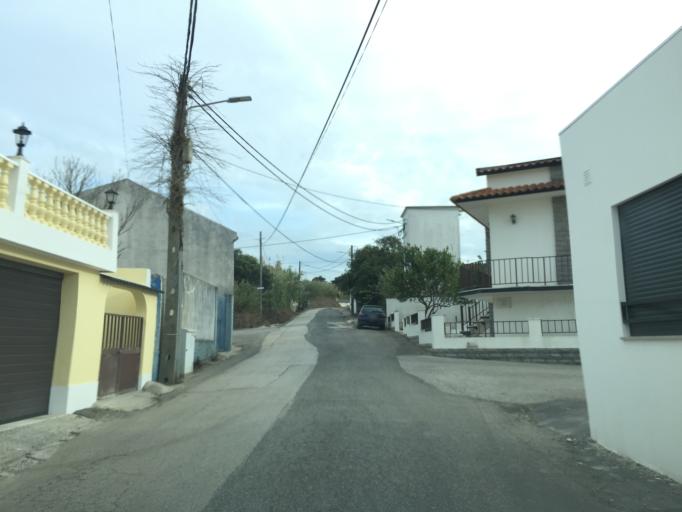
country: PT
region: Leiria
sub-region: Peniche
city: Atouguia da Baleia
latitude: 39.3382
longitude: -9.2988
